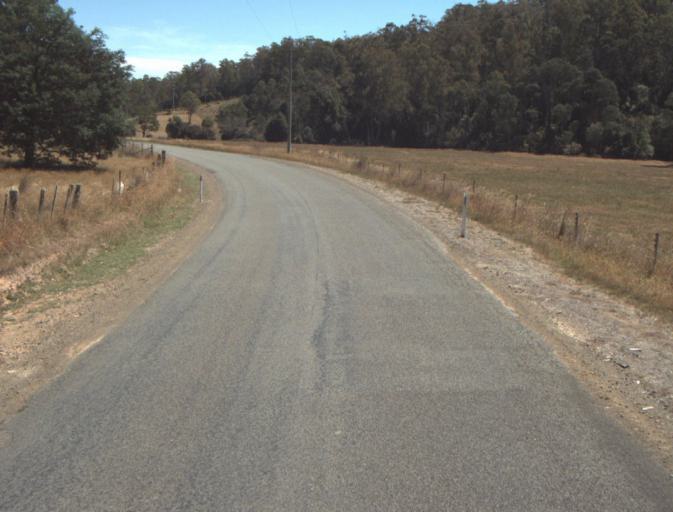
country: AU
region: Tasmania
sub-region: Dorset
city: Scottsdale
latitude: -41.3097
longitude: 147.3957
